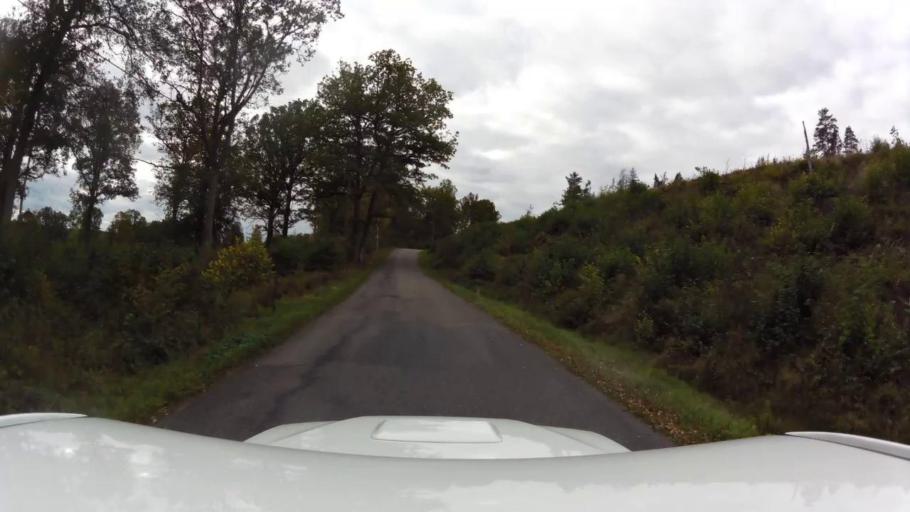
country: SE
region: OEstergoetland
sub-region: Kinda Kommun
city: Rimforsa
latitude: 58.2318
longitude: 15.6276
